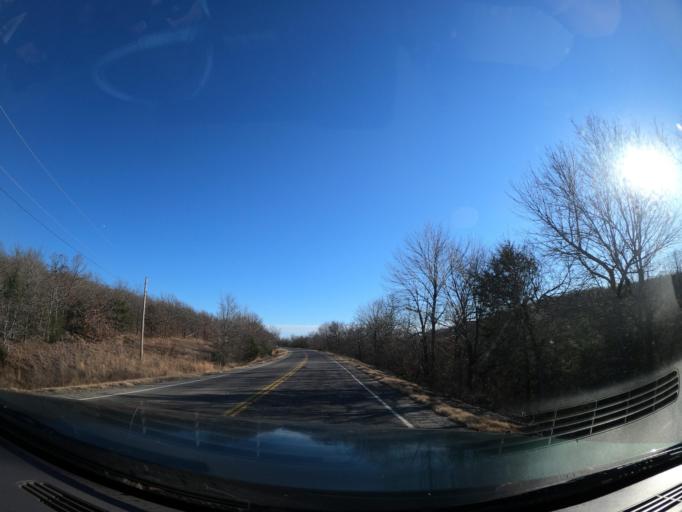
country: US
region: Oklahoma
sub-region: Pittsburg County
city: Longtown
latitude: 35.2206
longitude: -95.4285
